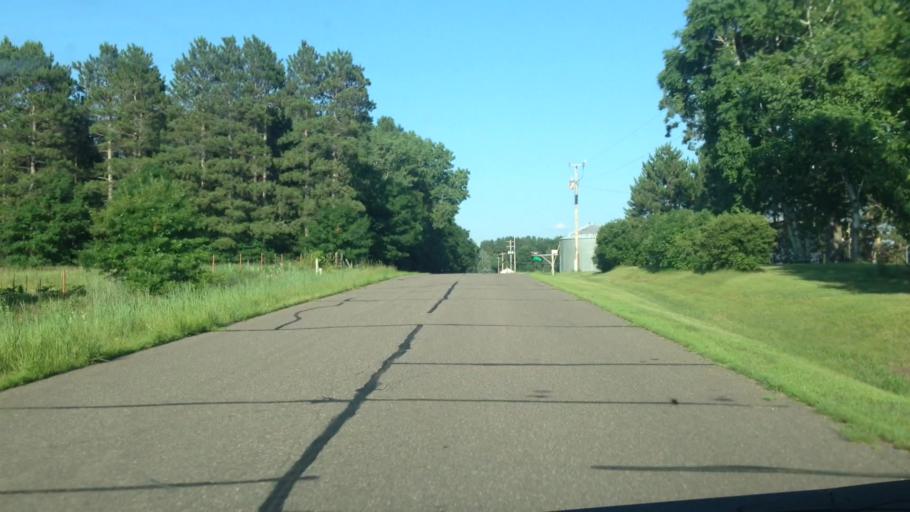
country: US
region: Minnesota
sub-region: Sherburne County
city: Big Lake
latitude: 45.4440
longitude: -93.7421
